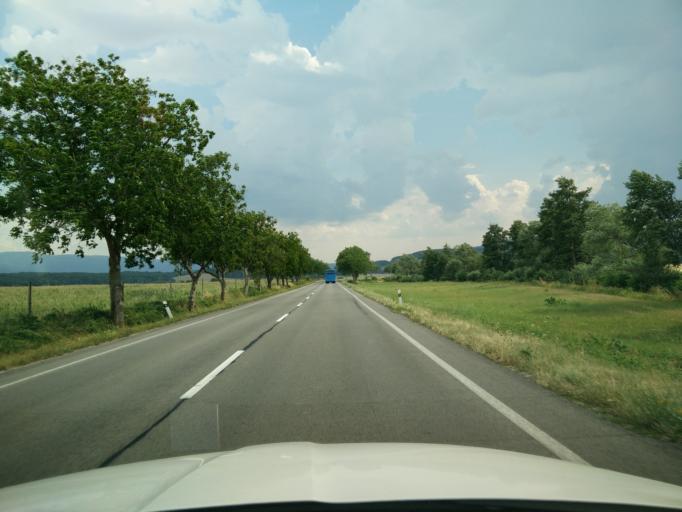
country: SK
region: Nitriansky
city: Novaky
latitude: 48.7407
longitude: 18.5016
